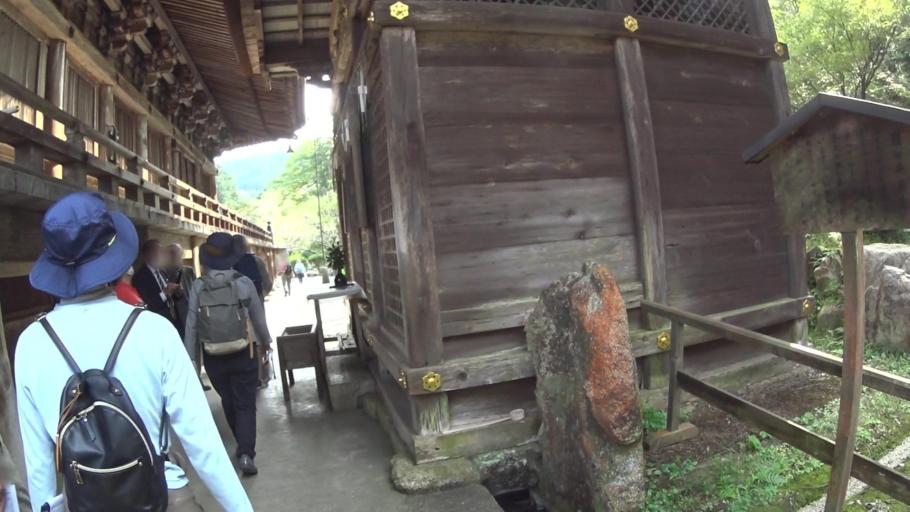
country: JP
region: Osaka
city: Kishiwada
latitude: 34.5095
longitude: 135.3420
